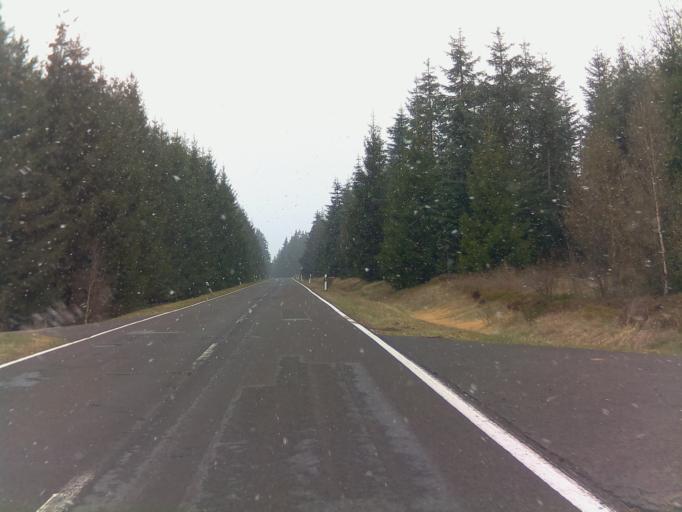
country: DE
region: Rheinland-Pfalz
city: Stipshausen
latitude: 49.8491
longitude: 7.2589
